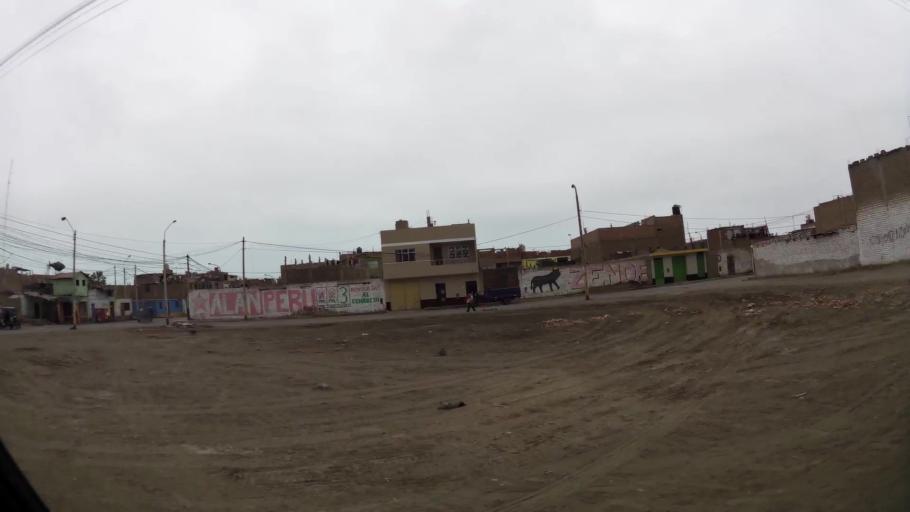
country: PE
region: Lima
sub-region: Barranca
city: Barranca
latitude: -10.7479
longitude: -77.7546
